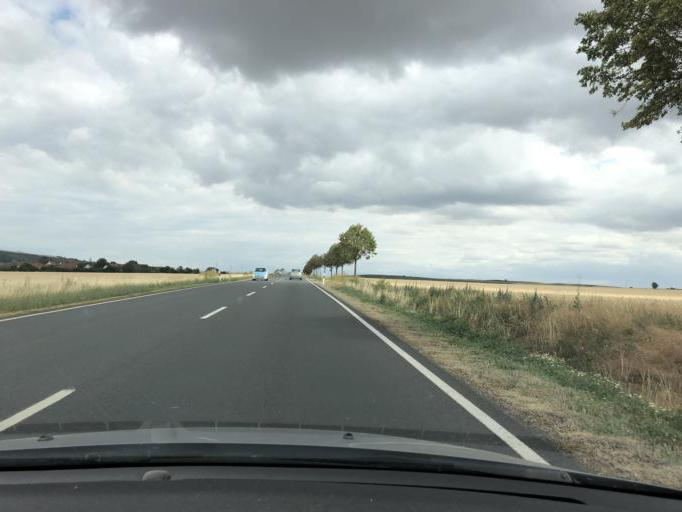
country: DE
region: Saxony-Anhalt
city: Erdeborn
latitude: 51.5009
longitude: 11.6178
